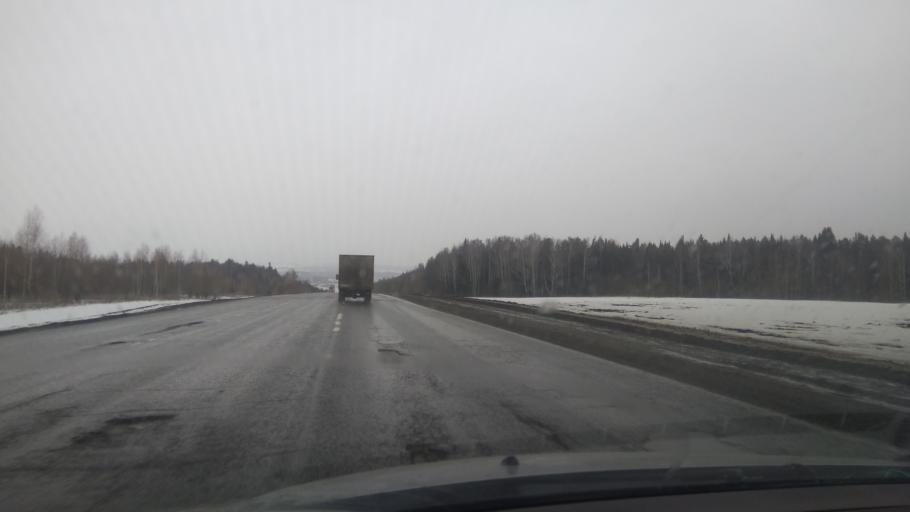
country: RU
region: Perm
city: Kungur
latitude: 57.3462
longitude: 56.9397
